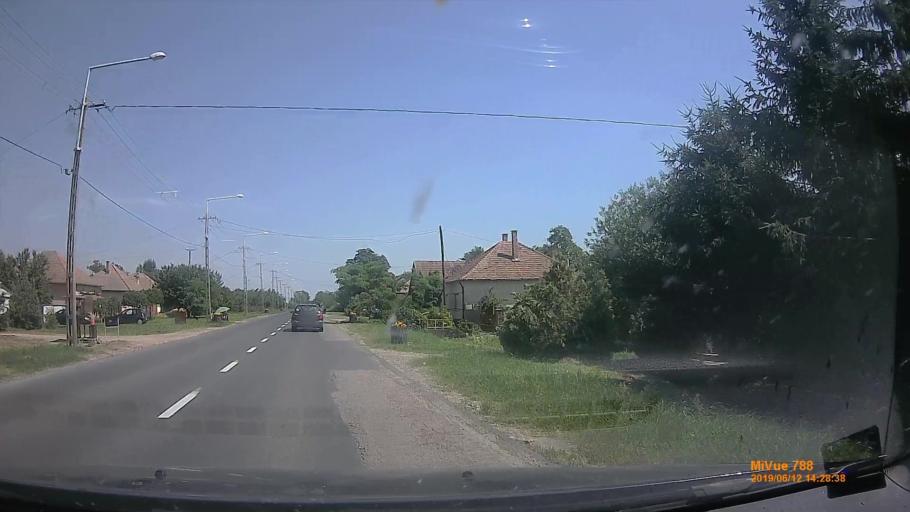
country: HU
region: Csongrad
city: Maroslele
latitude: 46.2119
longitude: 20.3653
